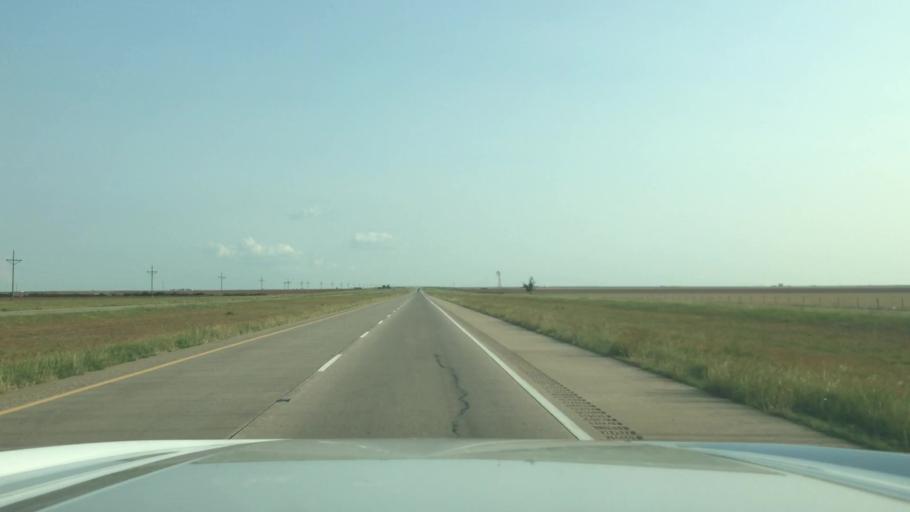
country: US
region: Texas
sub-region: Randall County
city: Canyon
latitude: 34.9173
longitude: -101.8487
